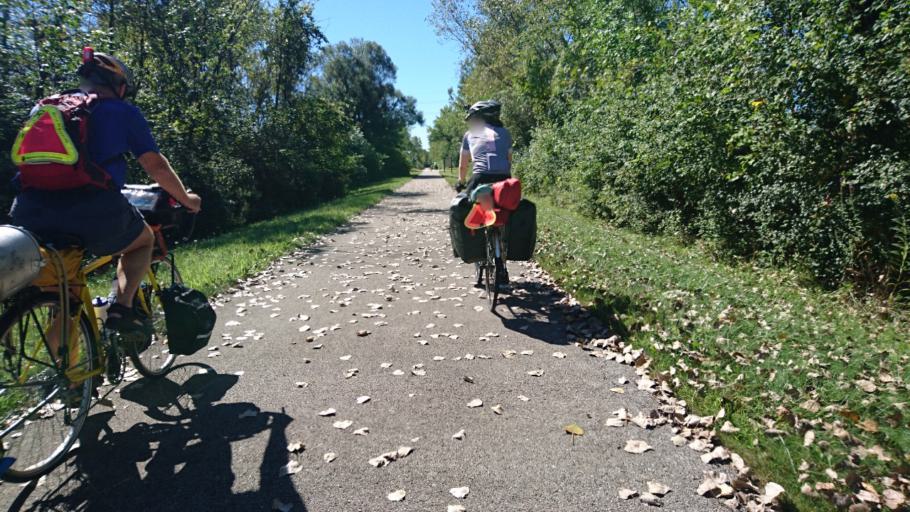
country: US
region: Illinois
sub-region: Cook County
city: Lansing
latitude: 41.5877
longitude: -87.5493
